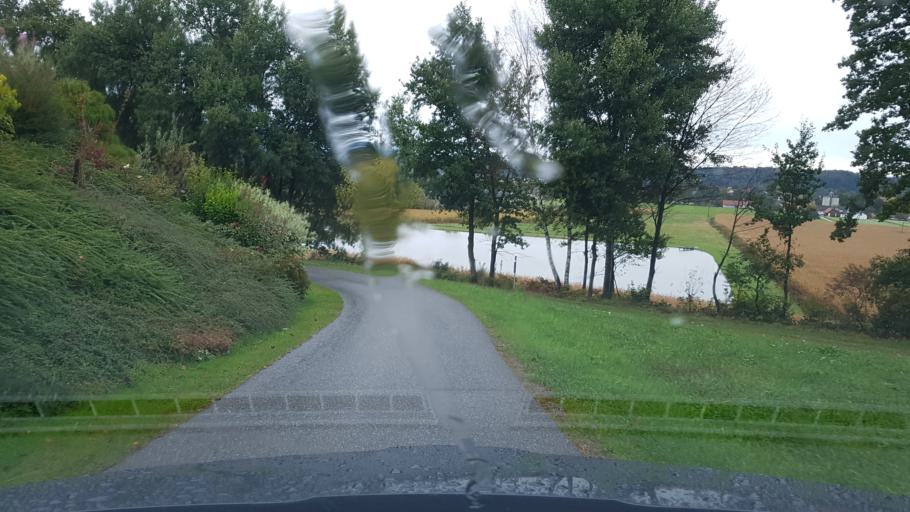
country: AT
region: Styria
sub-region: Politischer Bezirk Deutschlandsberg
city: Sankt Martin im Sulmtal
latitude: 46.7465
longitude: 15.2892
